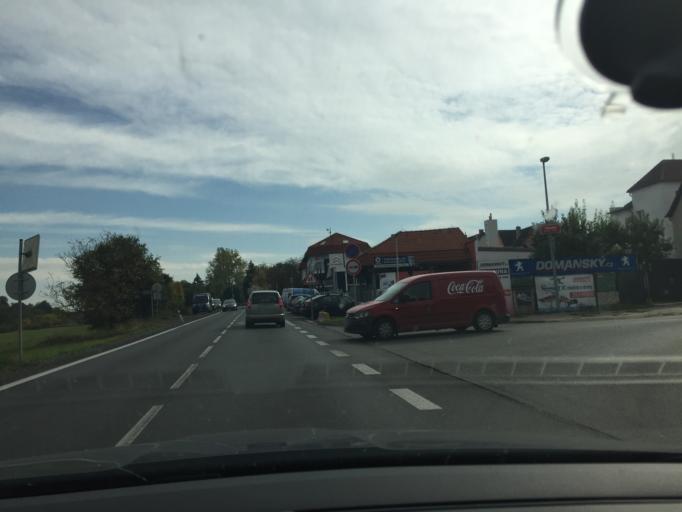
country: CZ
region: Praha
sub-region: Praha 14
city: Hostavice
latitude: 50.0880
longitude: 14.5546
